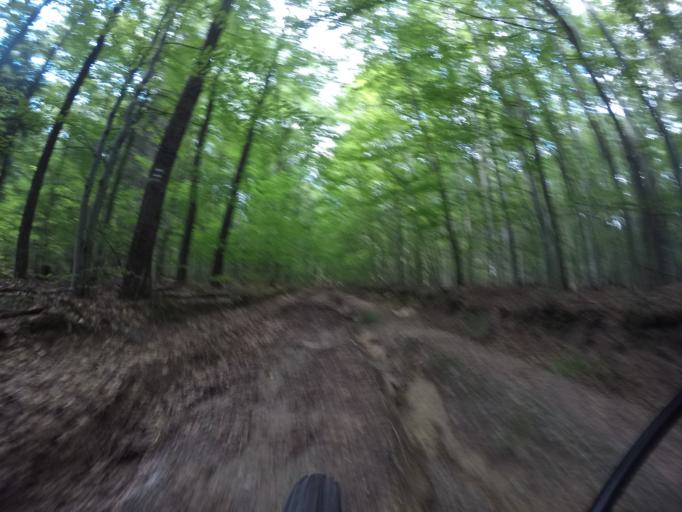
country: SK
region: Kosicky
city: Gelnica
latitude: 48.9240
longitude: 21.0369
